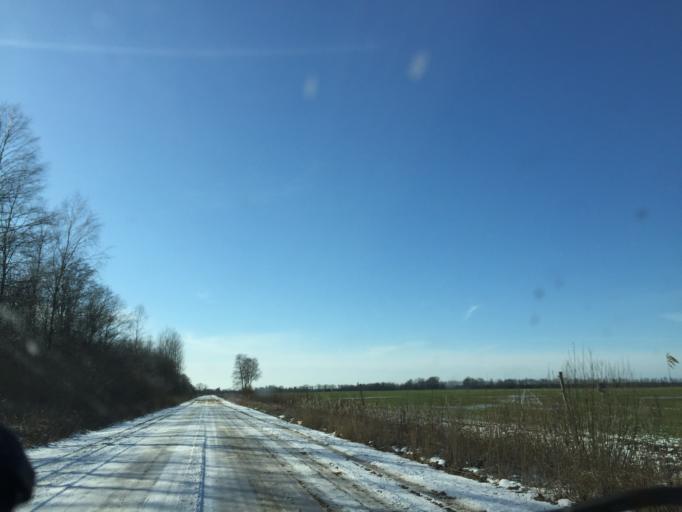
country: LV
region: Ventspils Rajons
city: Piltene
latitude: 57.2704
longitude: 21.6952
